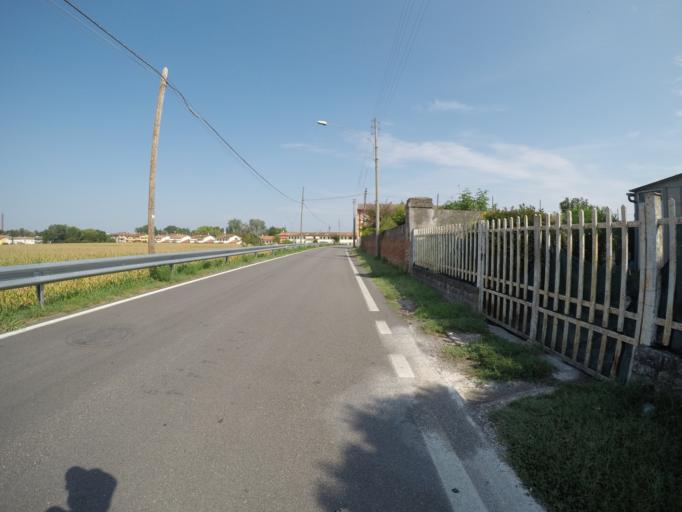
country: IT
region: Veneto
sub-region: Provincia di Rovigo
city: Lendinara
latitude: 45.0765
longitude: 11.6023
